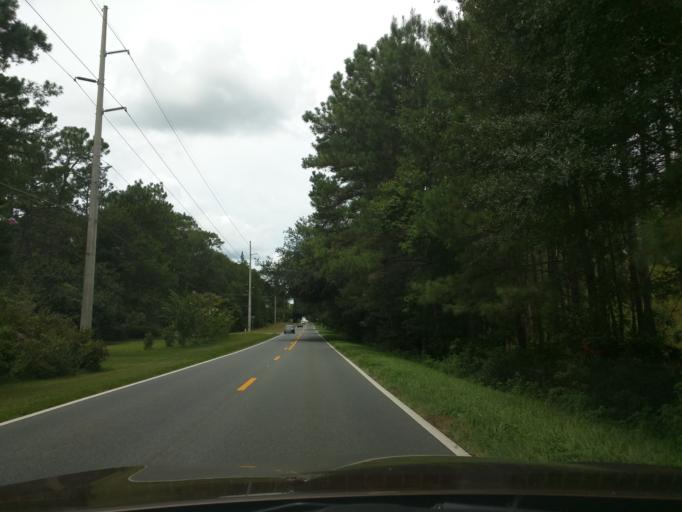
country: US
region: Florida
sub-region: Leon County
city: Tallahassee
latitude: 30.5595
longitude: -84.1862
